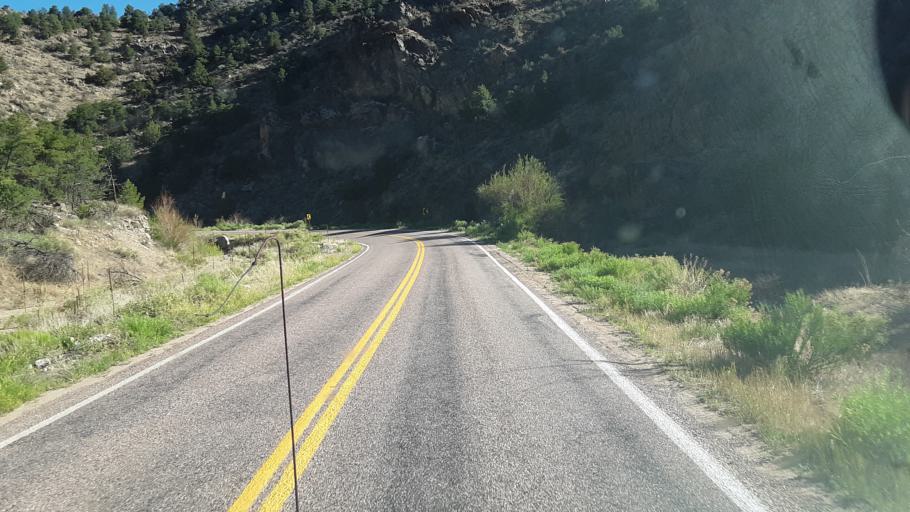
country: US
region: Colorado
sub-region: Fremont County
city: Canon City
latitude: 38.4324
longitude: -105.3925
